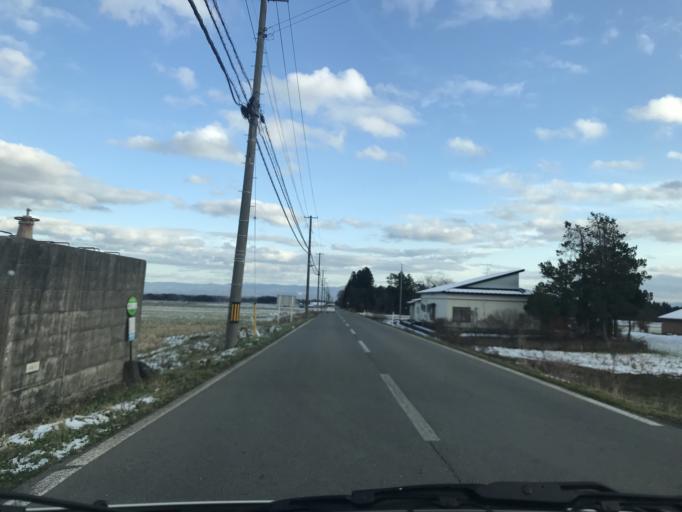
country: JP
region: Iwate
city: Kitakami
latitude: 39.2124
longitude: 141.0294
